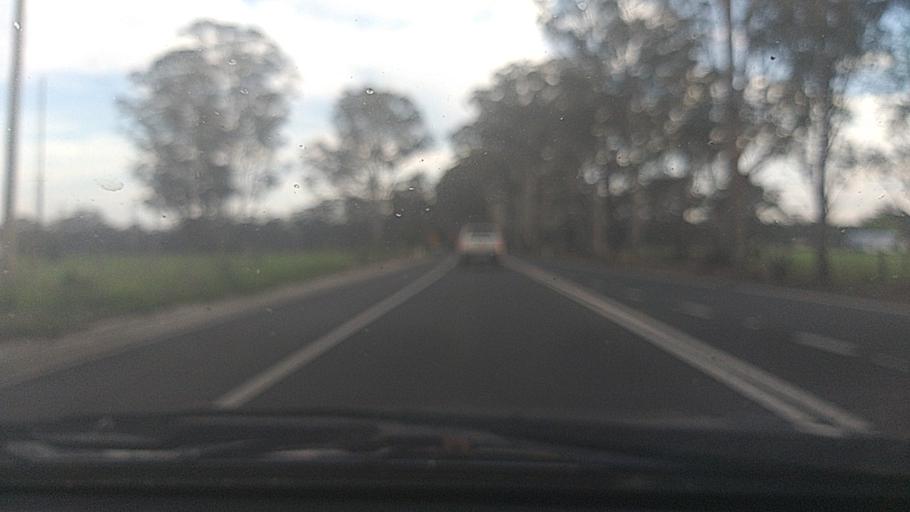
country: AU
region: New South Wales
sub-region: Wollondilly
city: Douglas Park
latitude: -34.1657
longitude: 150.7895
